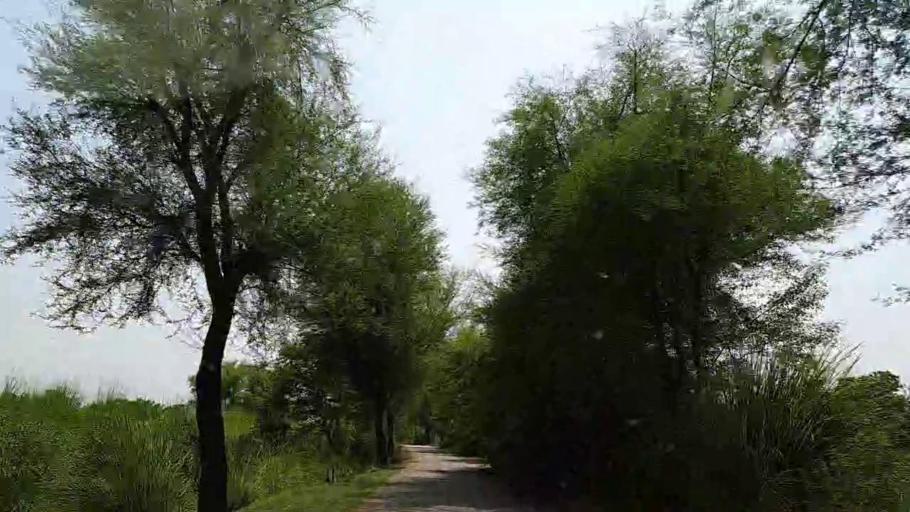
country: PK
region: Sindh
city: Adilpur
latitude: 27.9101
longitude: 69.3651
